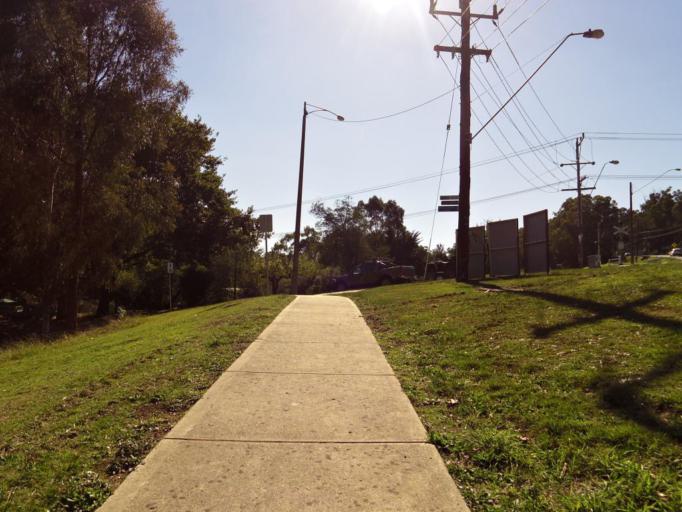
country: AU
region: Victoria
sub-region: Cardinia
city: Cockatoo
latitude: -37.9360
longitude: 145.4912
